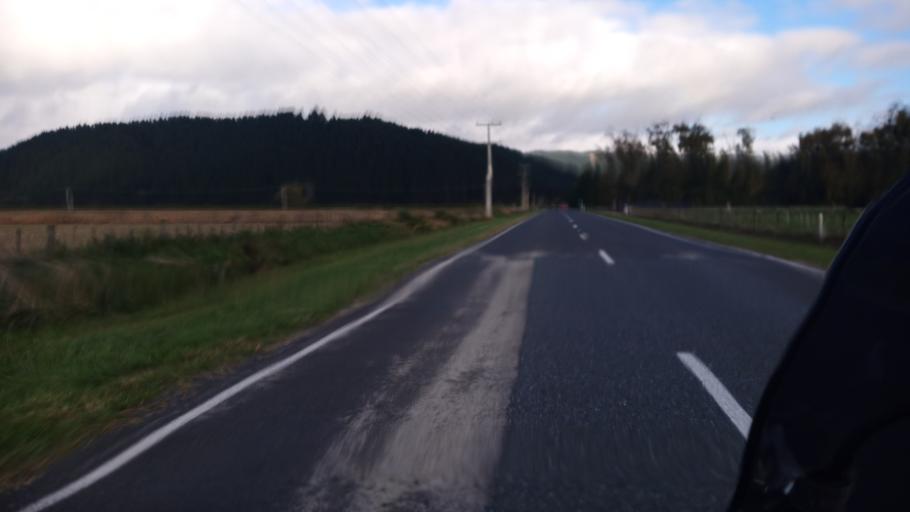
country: NZ
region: Gisborne
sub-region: Gisborne District
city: Gisborne
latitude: -38.6343
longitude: 177.8596
